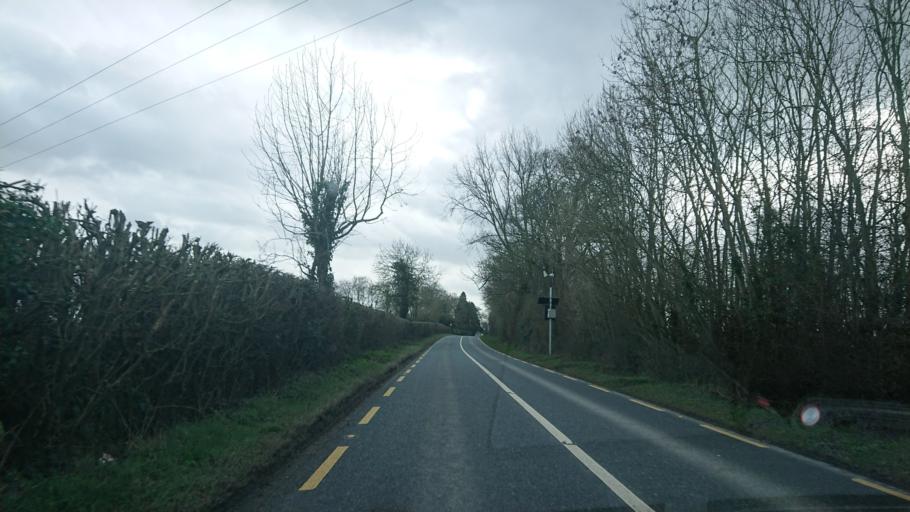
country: IE
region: Leinster
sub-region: Kildare
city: Naas
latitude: 53.1717
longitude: -6.6861
